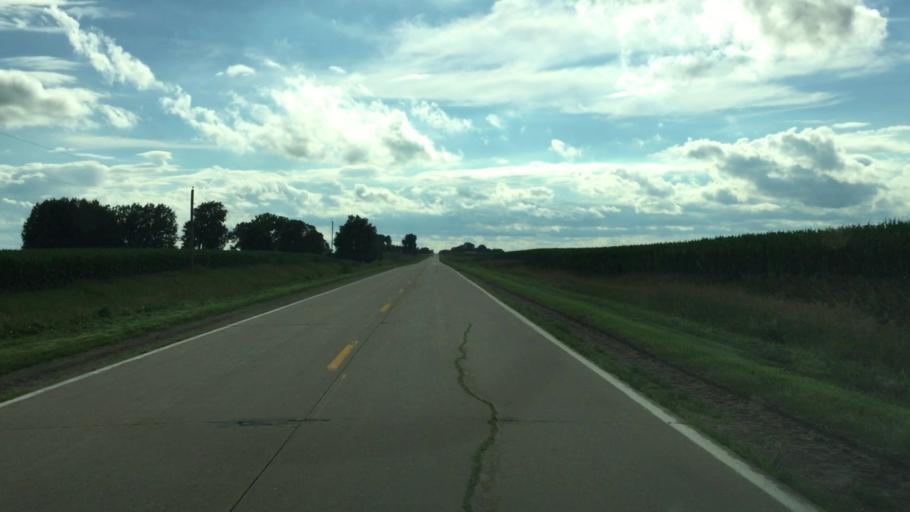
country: US
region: Iowa
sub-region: Jasper County
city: Prairie City
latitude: 41.5806
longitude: -93.1647
